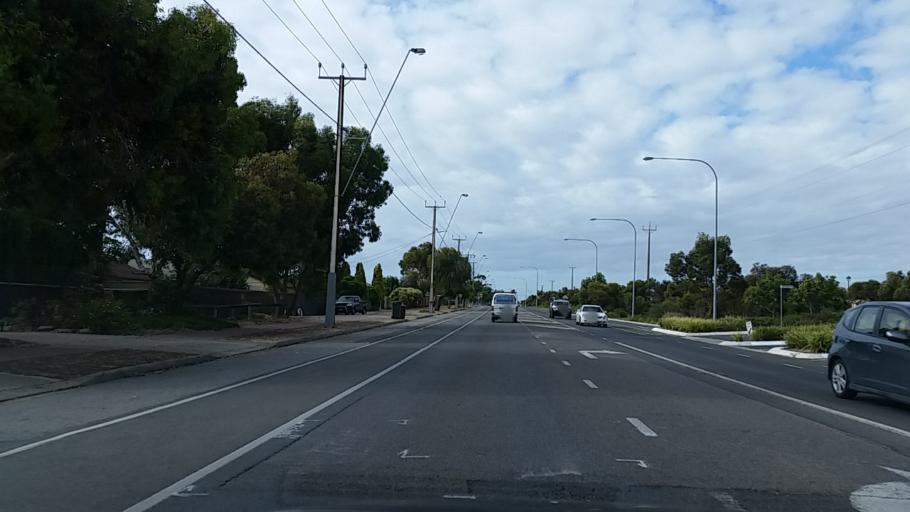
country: AU
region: South Australia
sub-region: Onkaparinga
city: Seaford
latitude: -35.1765
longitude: 138.4764
